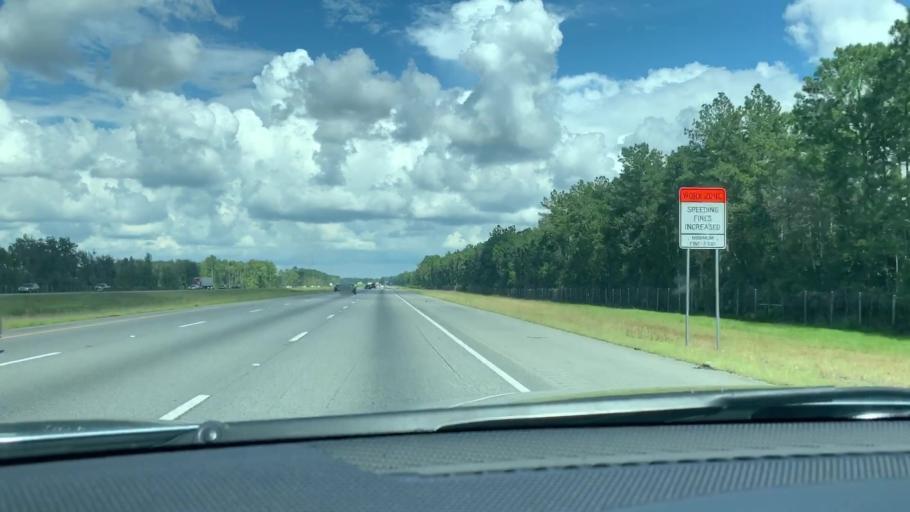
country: US
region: Georgia
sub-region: Glynn County
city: Brunswick
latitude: 31.0741
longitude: -81.6213
